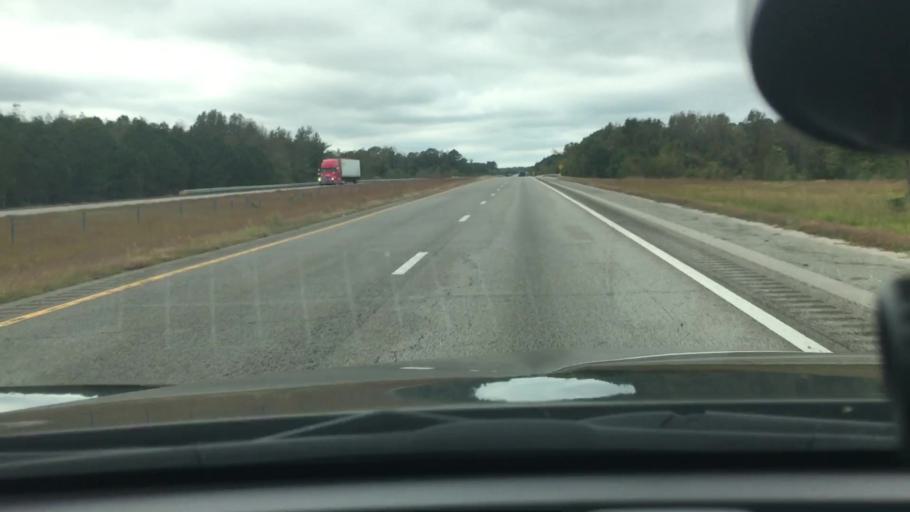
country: US
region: North Carolina
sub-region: Wilson County
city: Wilson
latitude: 35.6743
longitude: -77.9088
